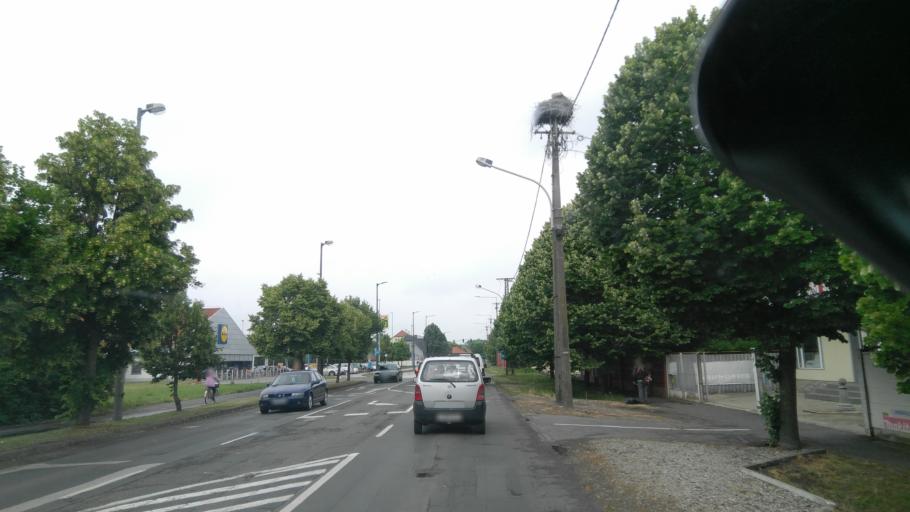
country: HU
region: Bekes
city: Bekescsaba
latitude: 46.6708
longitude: 21.1071
